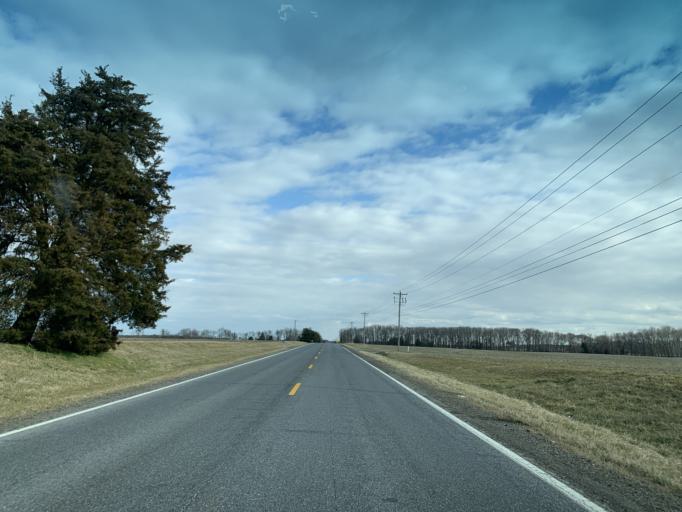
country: US
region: Maryland
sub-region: Queen Anne's County
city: Centreville
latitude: 39.0238
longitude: -76.0155
